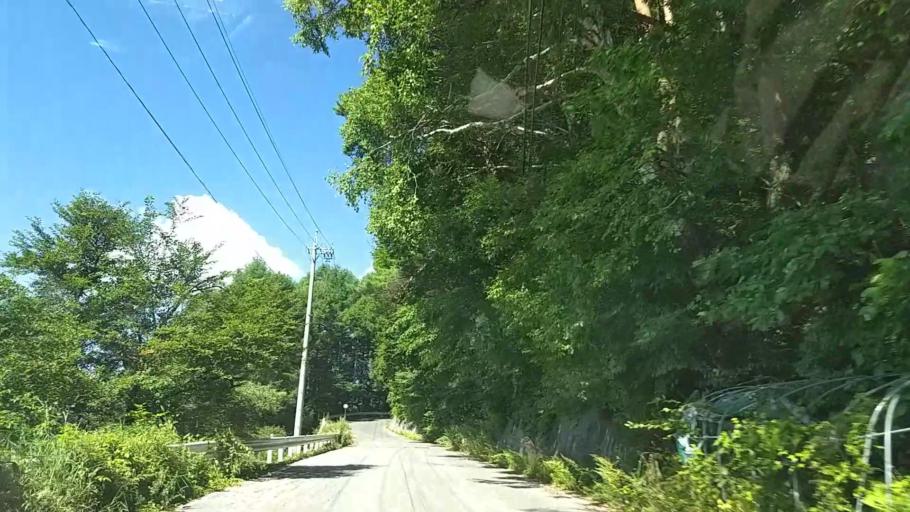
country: JP
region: Nagano
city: Matsumoto
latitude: 36.2103
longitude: 138.1011
